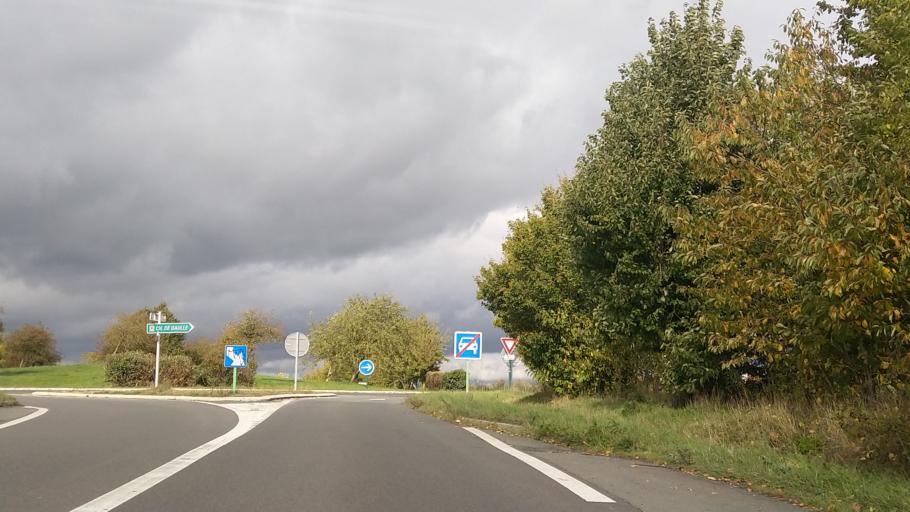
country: FR
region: Ile-de-France
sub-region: Departement du Val-d'Oise
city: Belloy-en-France
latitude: 49.0697
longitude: 2.3862
